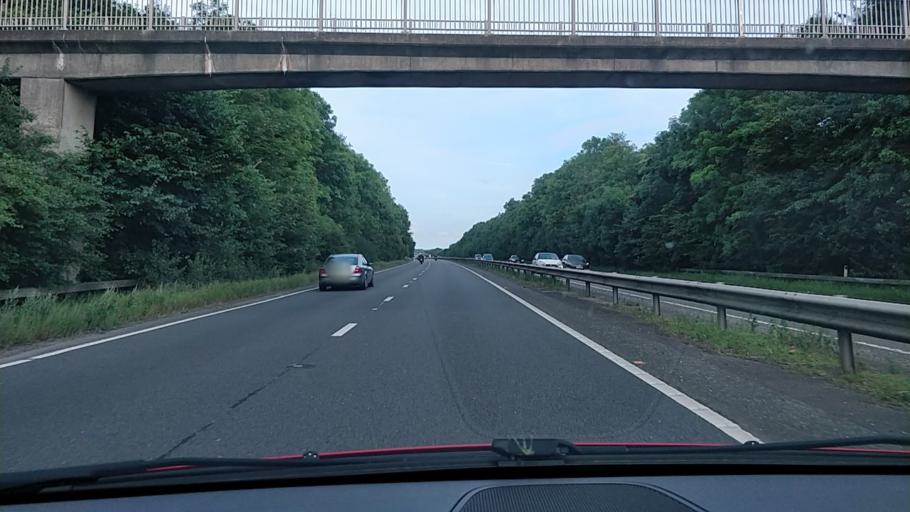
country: GB
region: Wales
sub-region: Wrexham
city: Rossett
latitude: 53.1613
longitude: -2.9588
